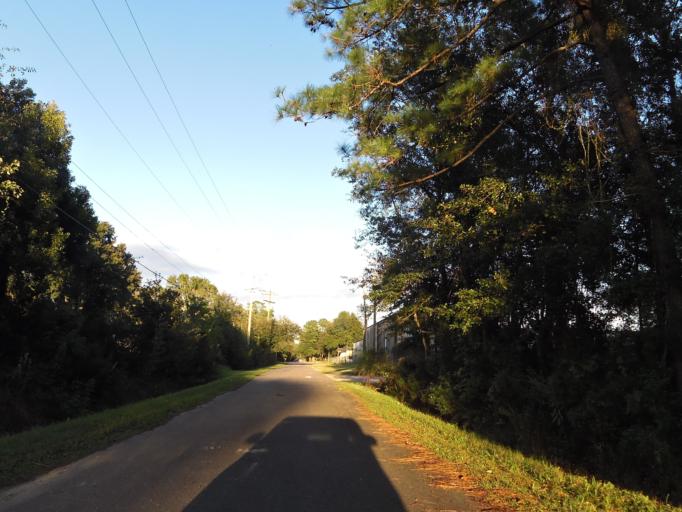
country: US
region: Florida
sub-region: Duval County
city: Jacksonville
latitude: 30.3549
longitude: -81.7368
